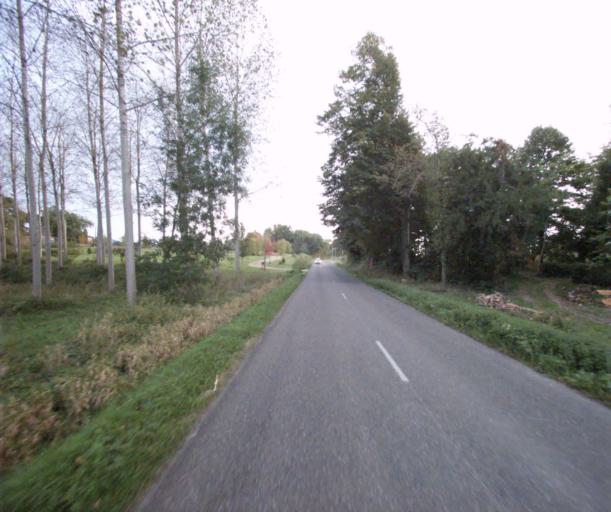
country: FR
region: Midi-Pyrenees
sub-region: Departement du Gers
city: Cazaubon
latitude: 43.9261
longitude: -0.0757
